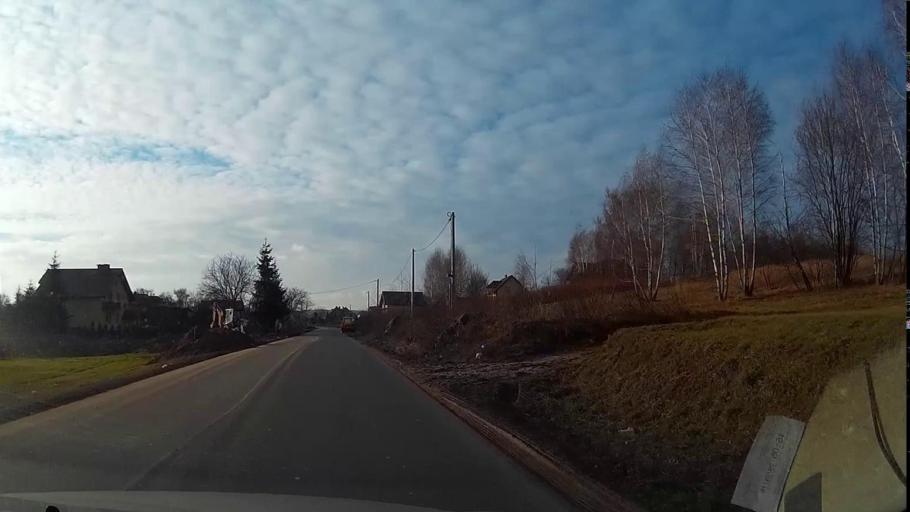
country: PL
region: Lesser Poland Voivodeship
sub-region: Powiat krakowski
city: Mnikow
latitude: 50.0595
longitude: 19.7462
